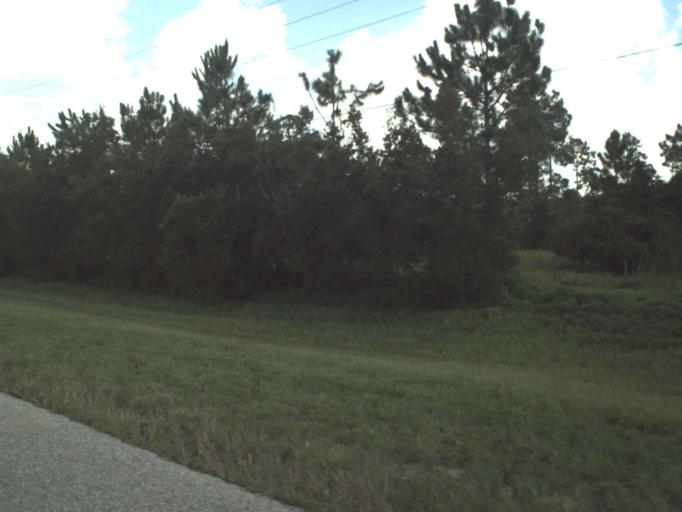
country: US
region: Florida
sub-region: Indian River County
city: Fellsmere
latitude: 27.6741
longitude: -80.8093
